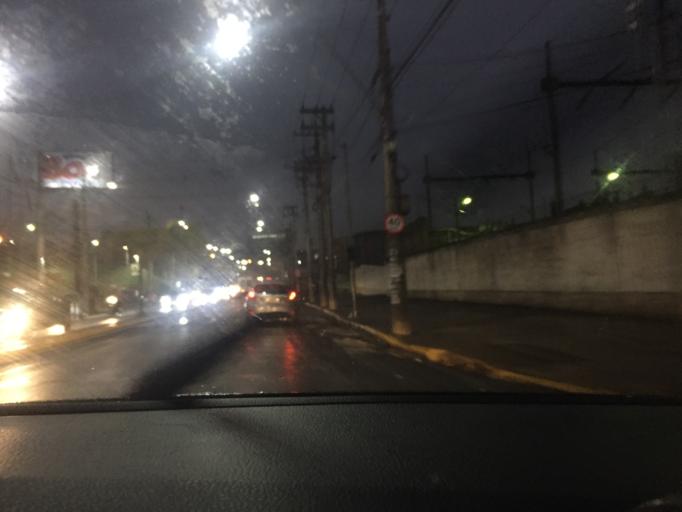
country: BR
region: Sao Paulo
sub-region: Varzea Paulista
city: Varzea Paulista
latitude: -23.2129
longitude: -46.8399
